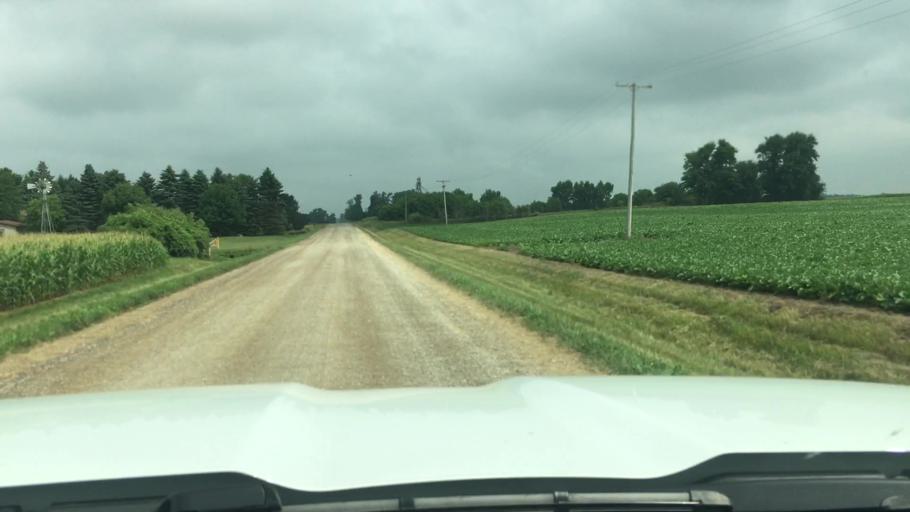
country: US
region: Michigan
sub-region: Sanilac County
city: Marlette
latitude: 43.3404
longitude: -82.9750
